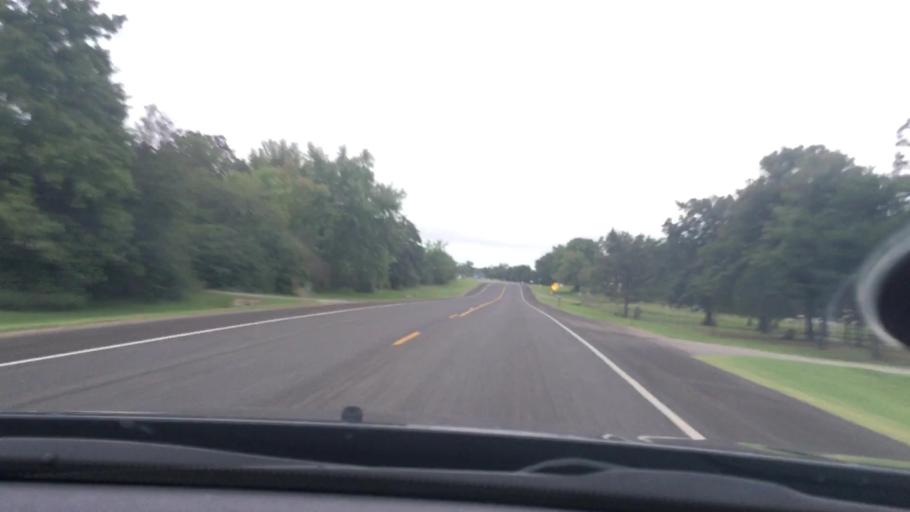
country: US
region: Oklahoma
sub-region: Sequoyah County
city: Vian
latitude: 35.5610
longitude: -94.9816
